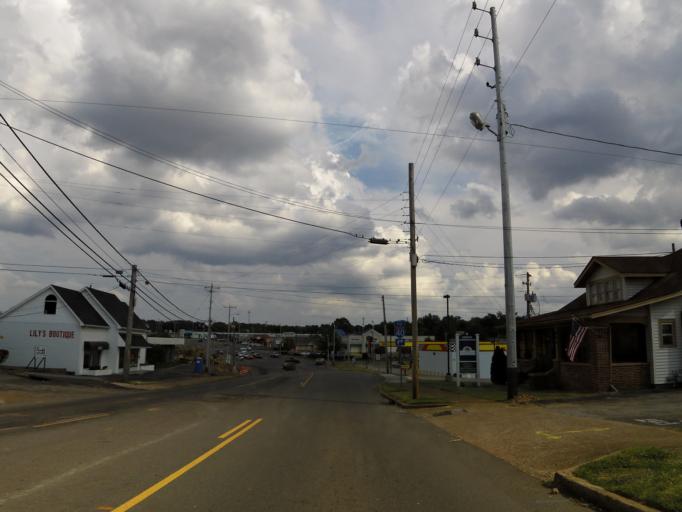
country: US
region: Tennessee
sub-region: Dickson County
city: Dickson
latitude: 36.0723
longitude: -87.3813
